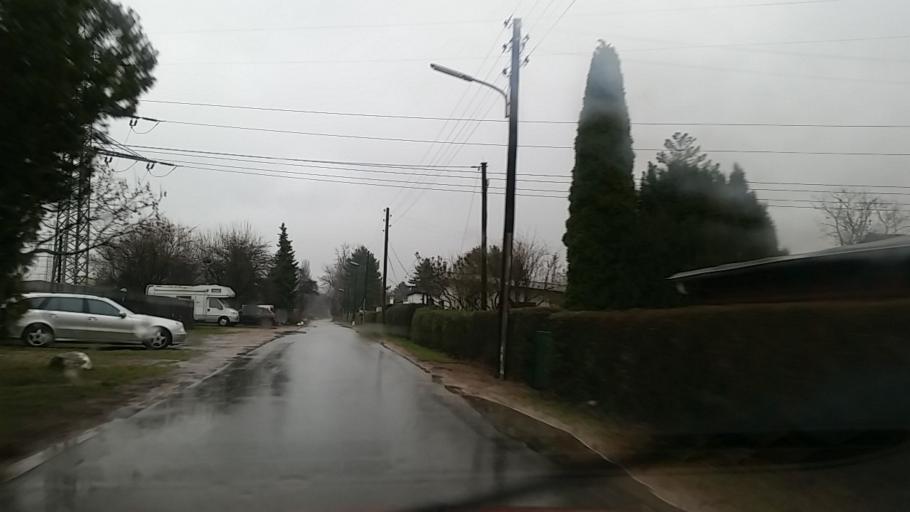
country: DE
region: Hamburg
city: Marienthal
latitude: 53.5388
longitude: 10.0775
